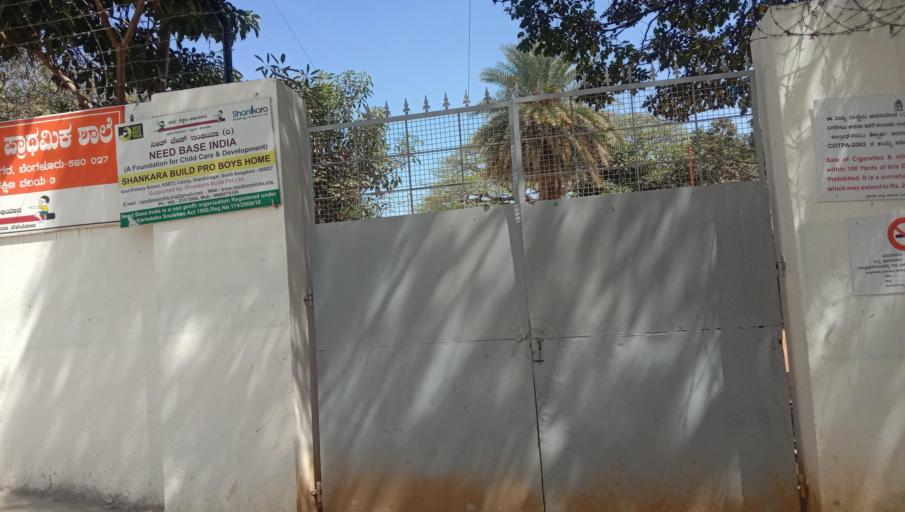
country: IN
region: Karnataka
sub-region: Bangalore Urban
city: Bangalore
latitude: 12.9537
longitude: 77.6003
